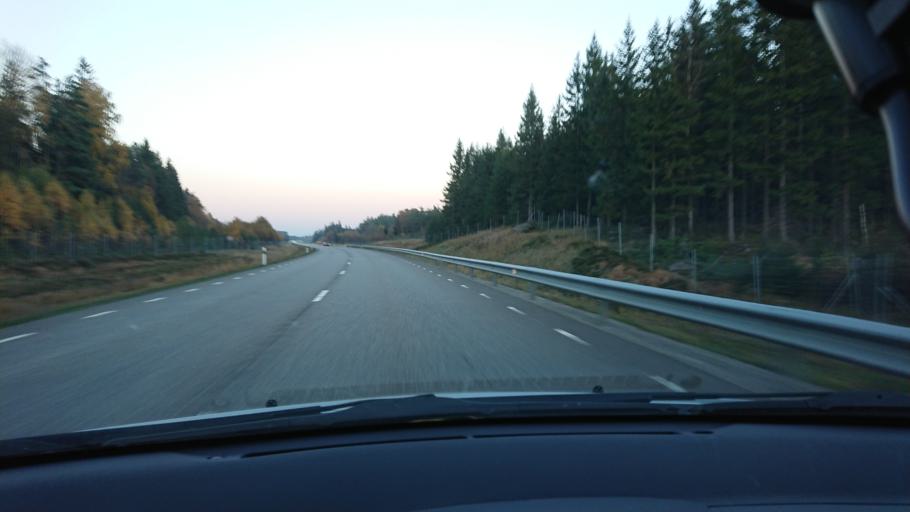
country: SE
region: Halland
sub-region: Laholms Kommun
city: Knared
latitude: 56.7406
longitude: 13.4727
